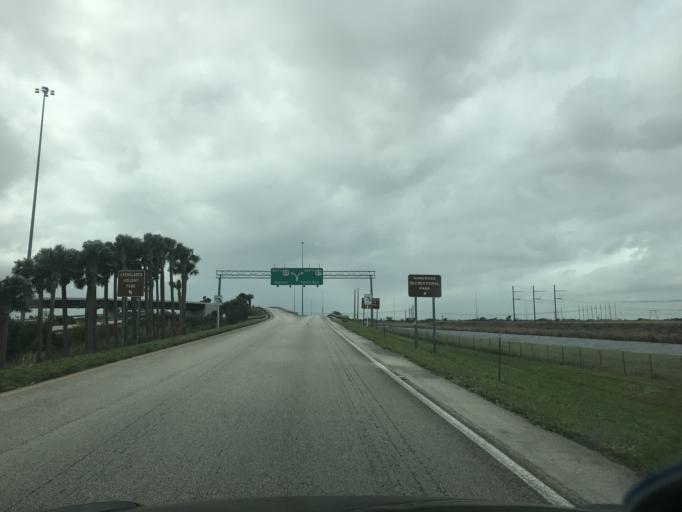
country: US
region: Florida
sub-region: Broward County
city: Weston
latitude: 26.1441
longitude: -80.4363
